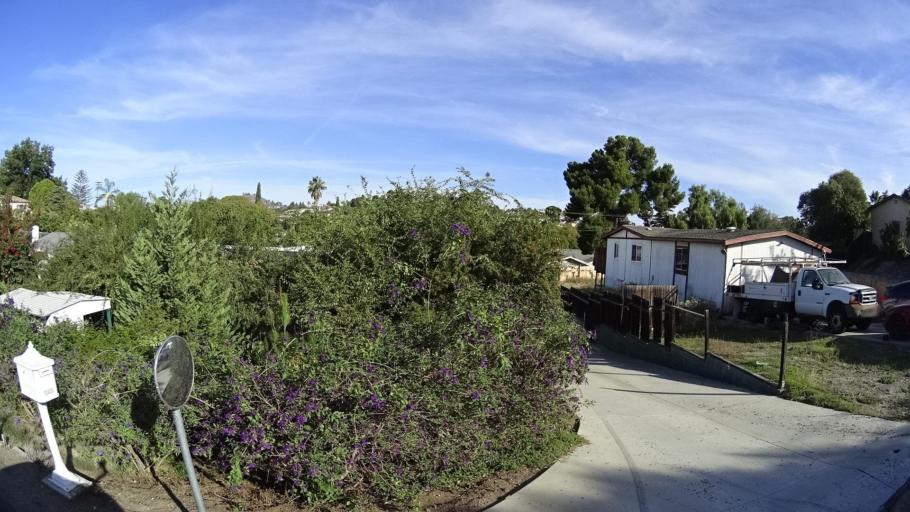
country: US
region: California
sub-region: San Diego County
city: Casa de Oro-Mount Helix
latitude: 32.7412
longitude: -116.9674
